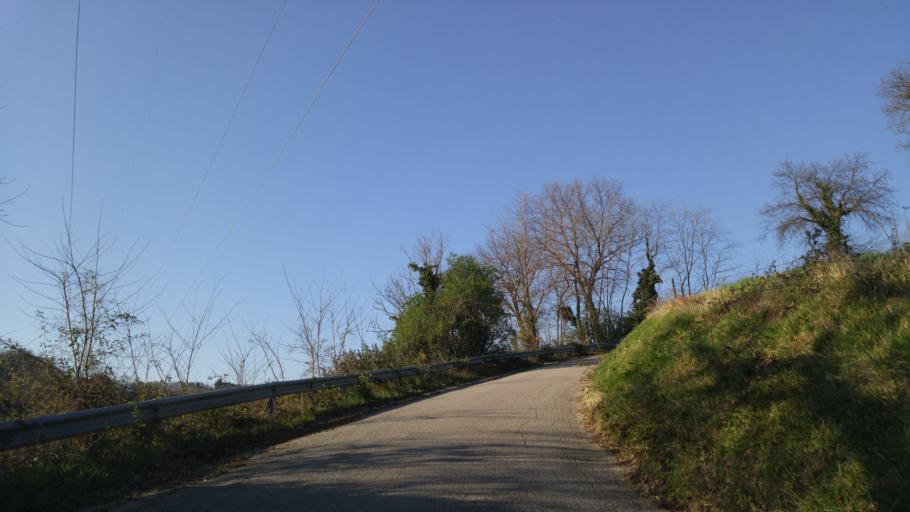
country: IT
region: The Marches
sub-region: Provincia di Pesaro e Urbino
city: Fenile
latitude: 43.8479
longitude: 12.9190
